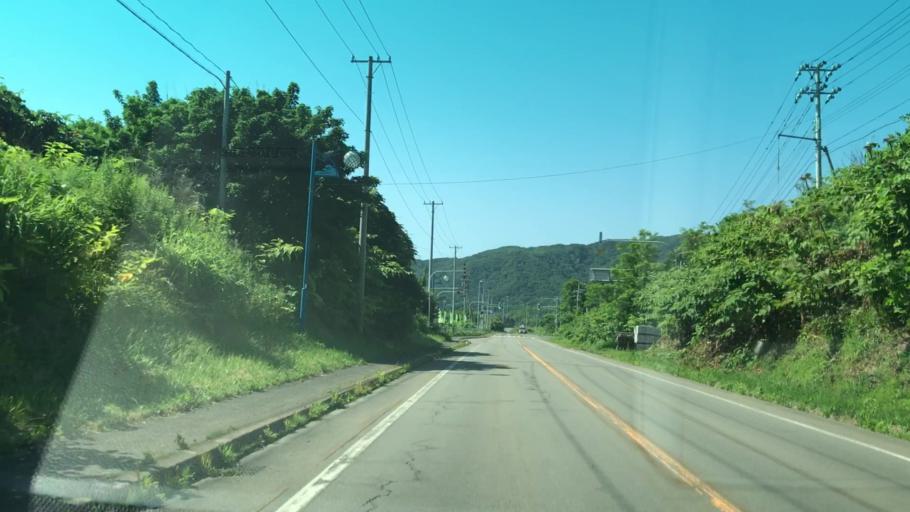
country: JP
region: Hokkaido
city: Iwanai
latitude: 43.0696
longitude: 140.4921
